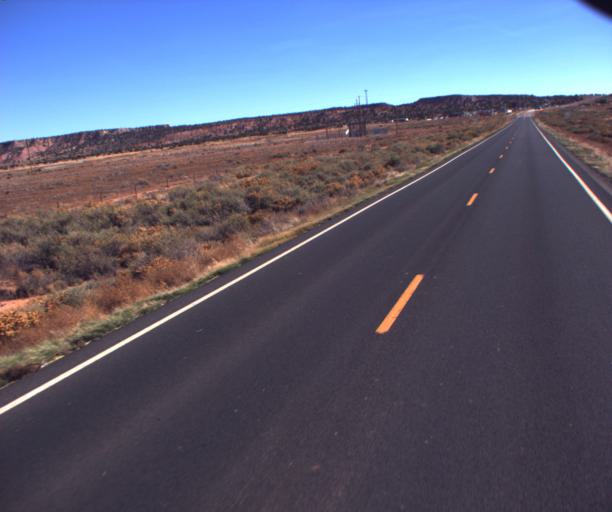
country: US
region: Arizona
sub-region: Apache County
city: Ganado
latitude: 35.7593
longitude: -109.6329
